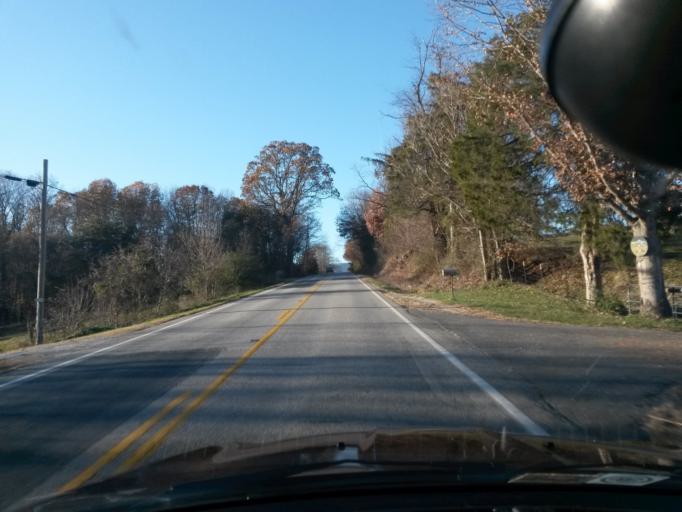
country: US
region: Virginia
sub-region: Amherst County
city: Amherst
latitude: 37.6482
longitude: -79.1301
